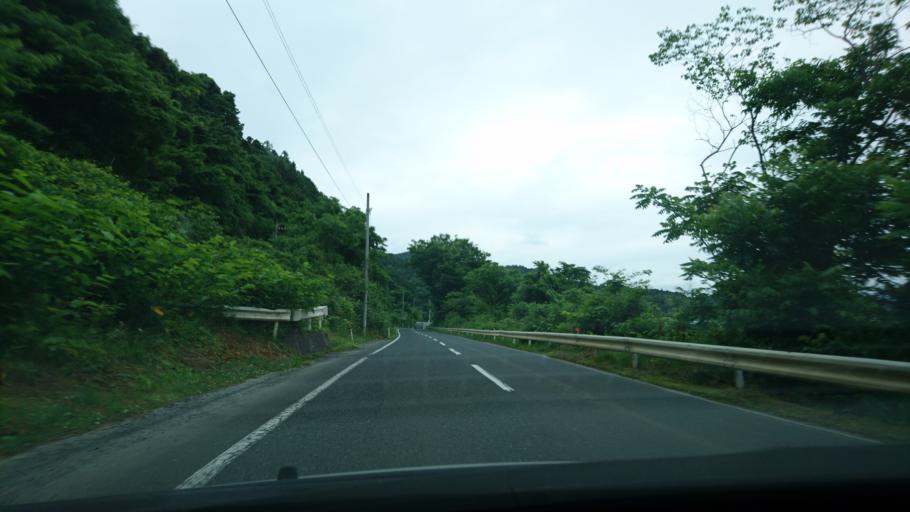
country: JP
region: Iwate
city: Ichinoseki
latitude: 38.9716
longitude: 141.2388
